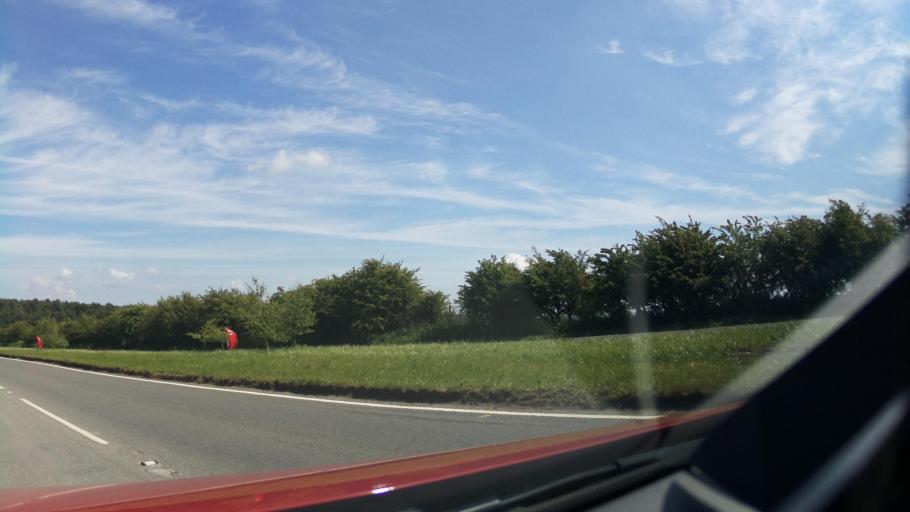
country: GB
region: England
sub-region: North Lincolnshire
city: Manton
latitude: 53.5138
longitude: -0.5801
